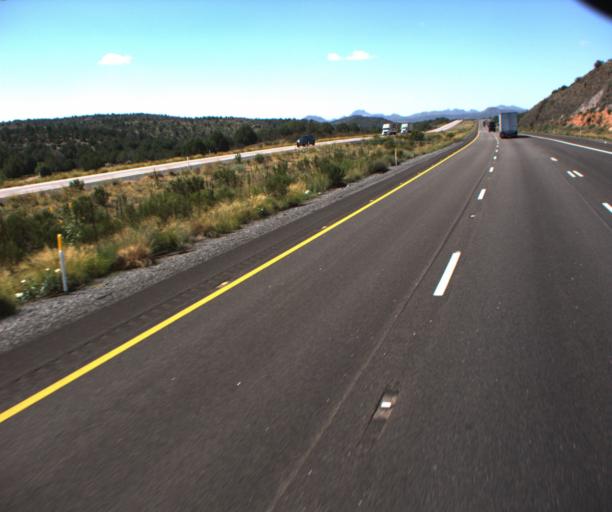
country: US
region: Arizona
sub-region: Mohave County
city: Peach Springs
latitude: 35.2020
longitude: -113.3023
